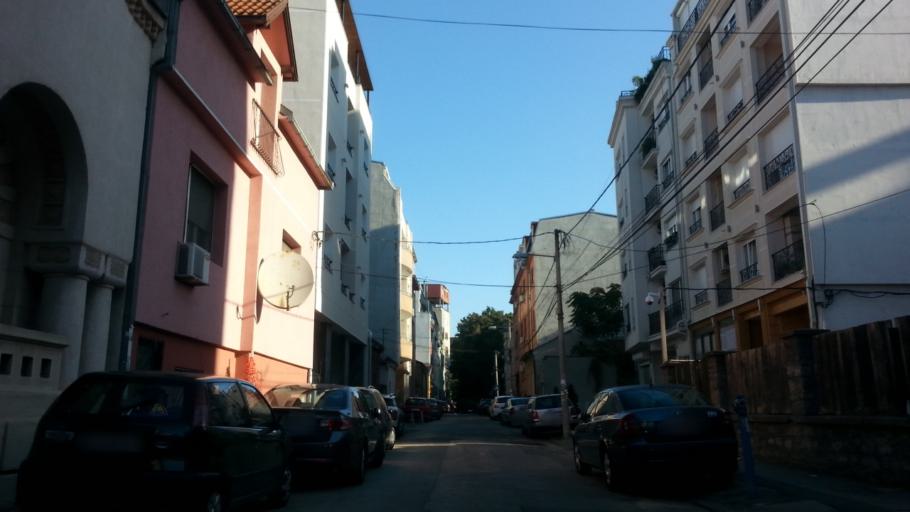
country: RS
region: Central Serbia
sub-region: Belgrade
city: Vracar
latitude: 44.7961
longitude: 20.4928
